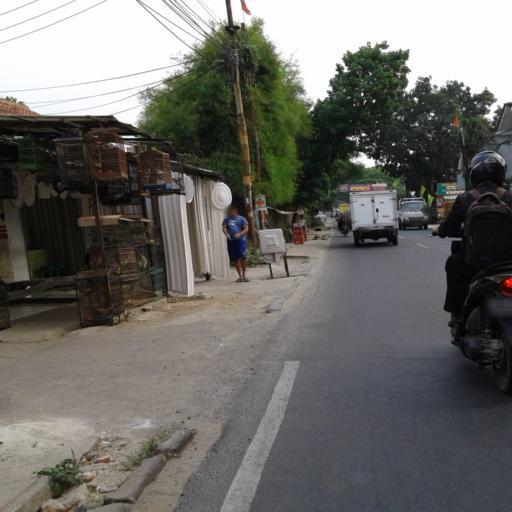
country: ID
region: West Java
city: Sawangan
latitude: -6.3987
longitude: 106.7718
